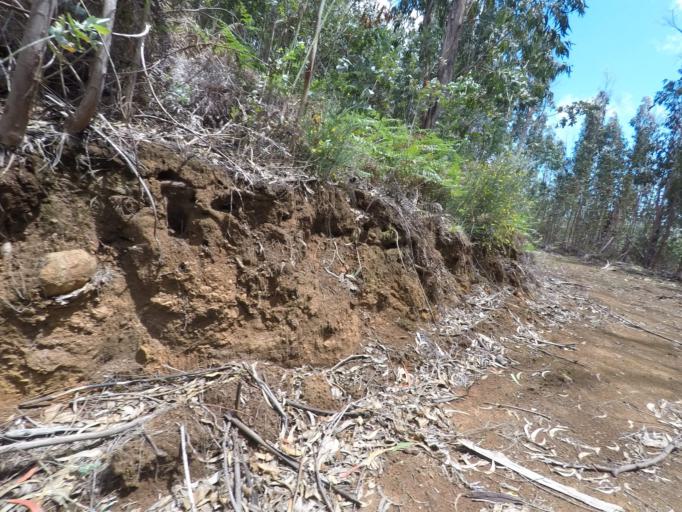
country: PT
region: Madeira
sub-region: Calheta
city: Estreito da Calheta
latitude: 32.7483
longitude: -17.1957
